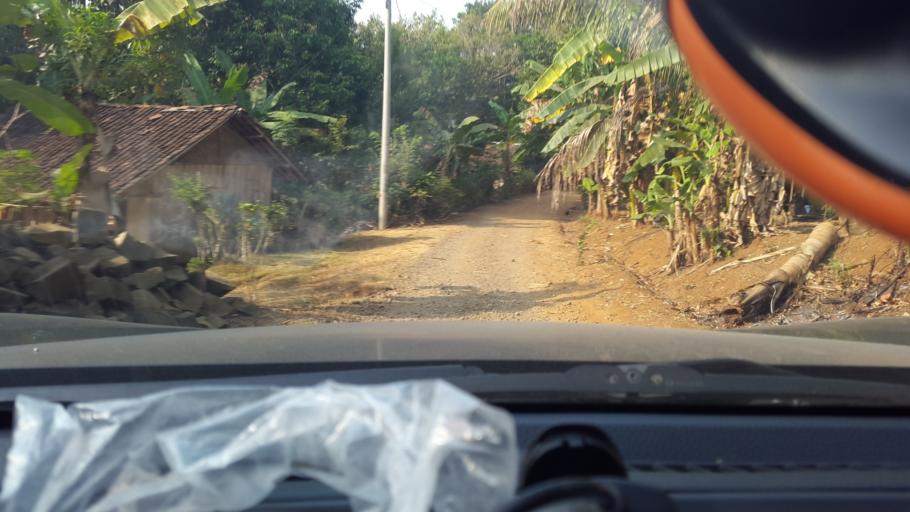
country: ID
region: West Java
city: Cikupa
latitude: -7.3449
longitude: 106.6991
